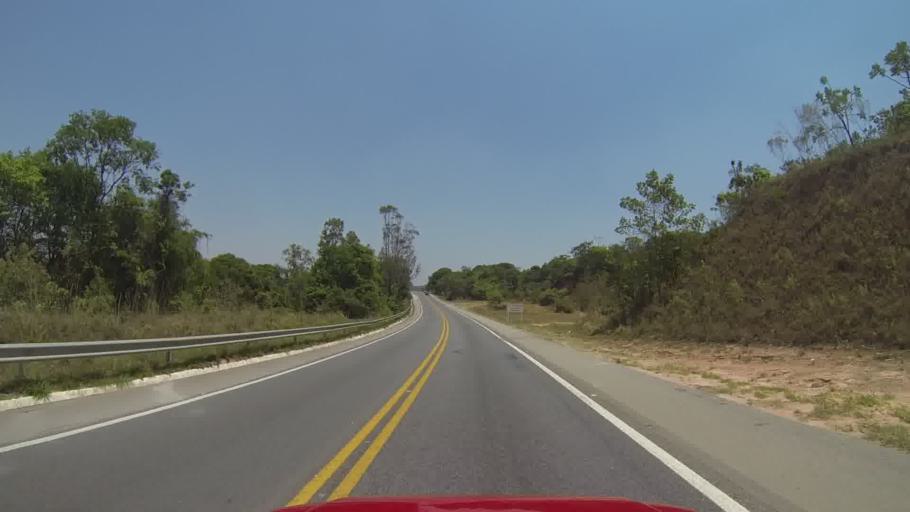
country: BR
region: Minas Gerais
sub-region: Itapecerica
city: Itapecerica
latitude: -20.2805
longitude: -45.1343
